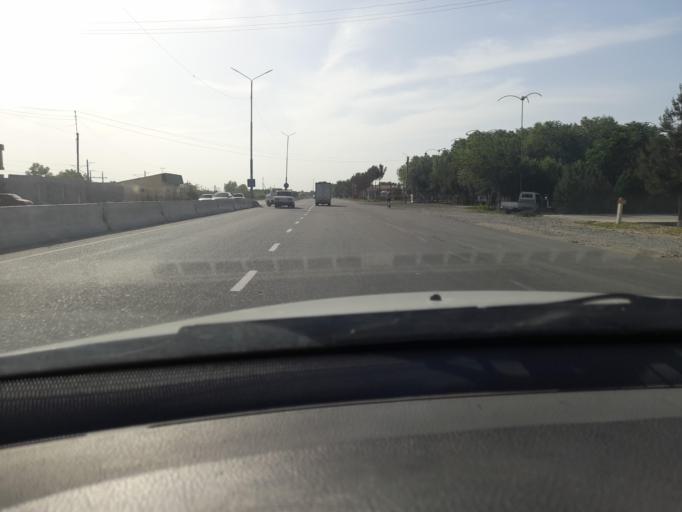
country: UZ
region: Samarqand
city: Kattaqo'rg'on
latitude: 39.9233
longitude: 66.2296
